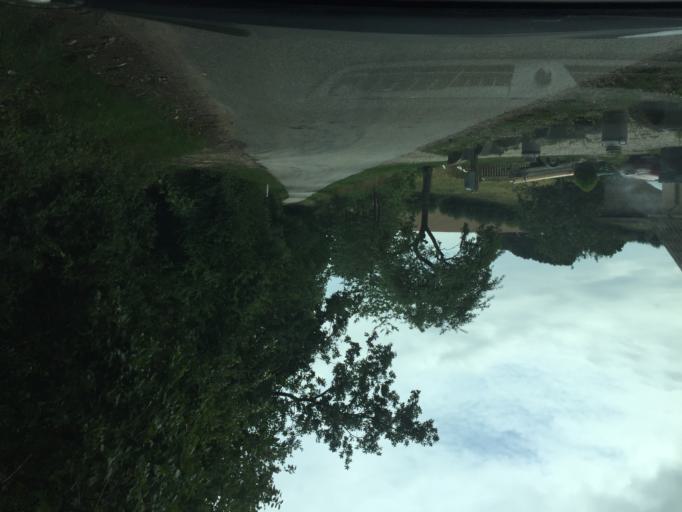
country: DK
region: South Denmark
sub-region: Assens Kommune
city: Arup
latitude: 55.3823
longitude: 10.0352
